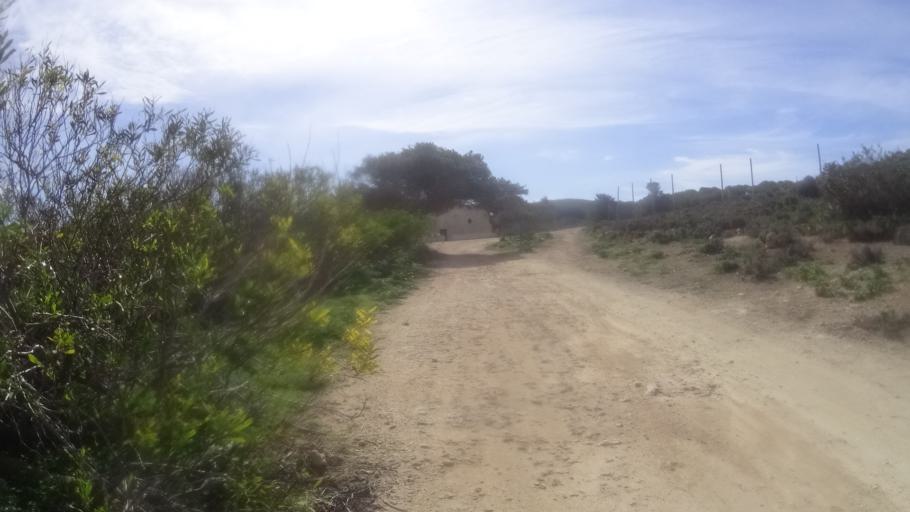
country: MT
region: Il-Qala
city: Qala
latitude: 36.0158
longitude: 14.3360
